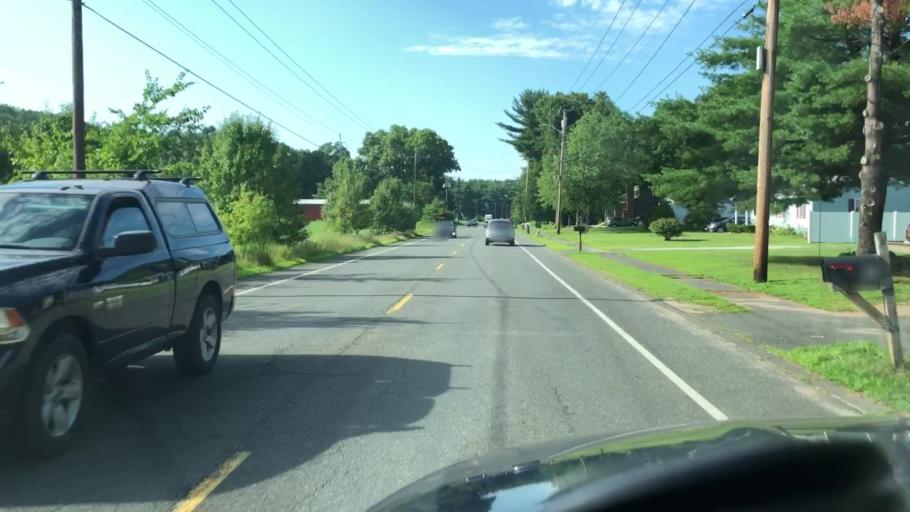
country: US
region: Massachusetts
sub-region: Hampshire County
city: Southampton
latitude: 42.2109
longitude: -72.6901
